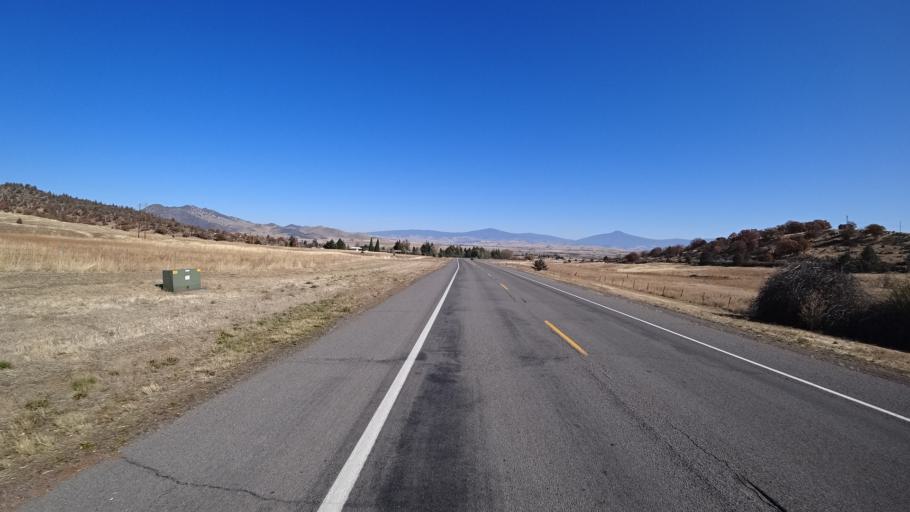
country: US
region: California
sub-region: Siskiyou County
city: Yreka
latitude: 41.7412
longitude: -122.6077
